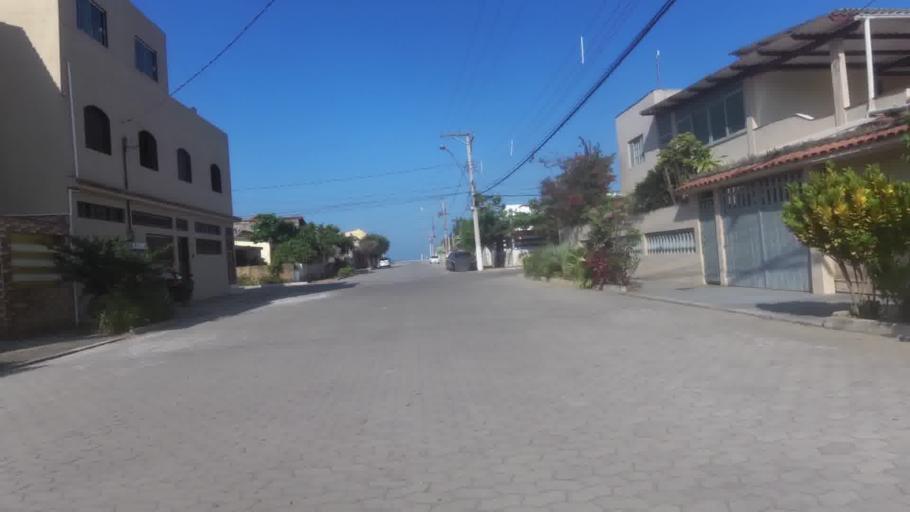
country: BR
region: Espirito Santo
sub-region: Itapemirim
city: Itapemirim
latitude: -21.0166
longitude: -40.8117
